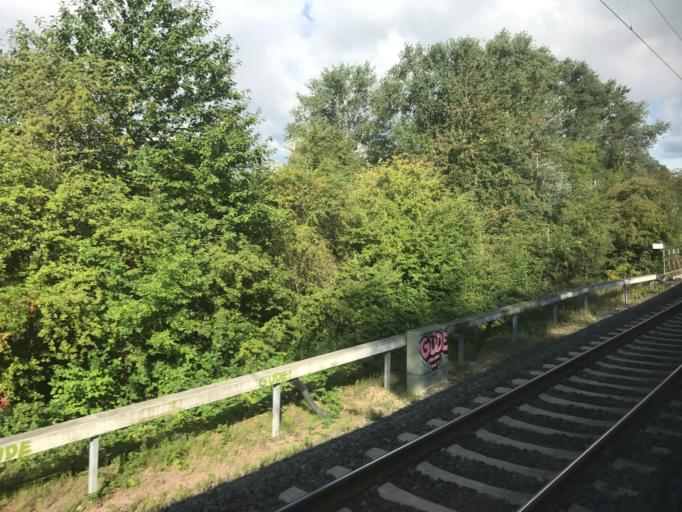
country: DE
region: Hesse
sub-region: Regierungsbezirk Darmstadt
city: Friedberg
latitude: 50.3238
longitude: 8.7722
